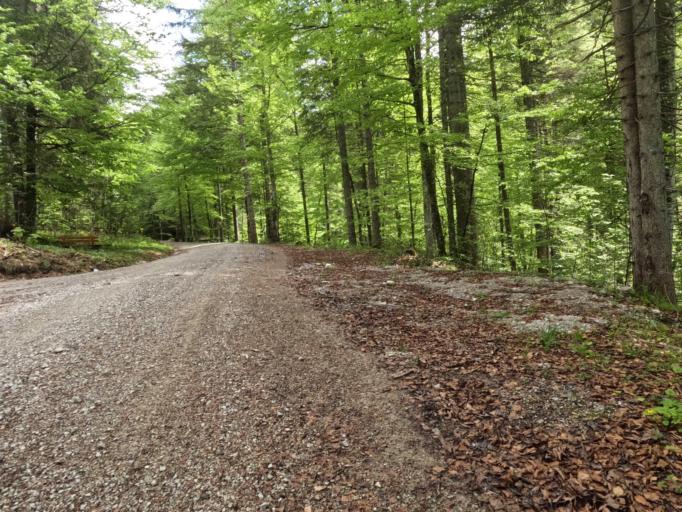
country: AT
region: Salzburg
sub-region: Politischer Bezirk Zell am See
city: Unken
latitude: 47.7153
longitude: 12.7000
